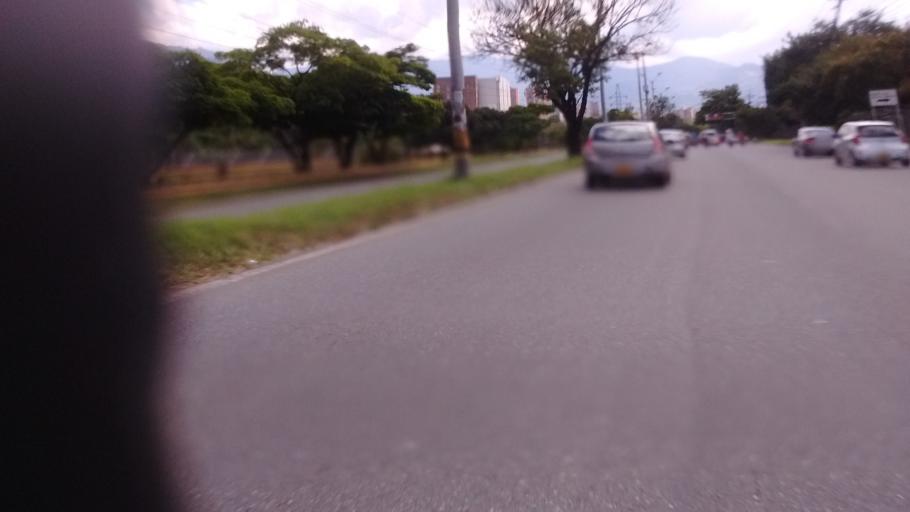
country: CO
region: Antioquia
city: Itagui
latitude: 6.2019
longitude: -75.5801
